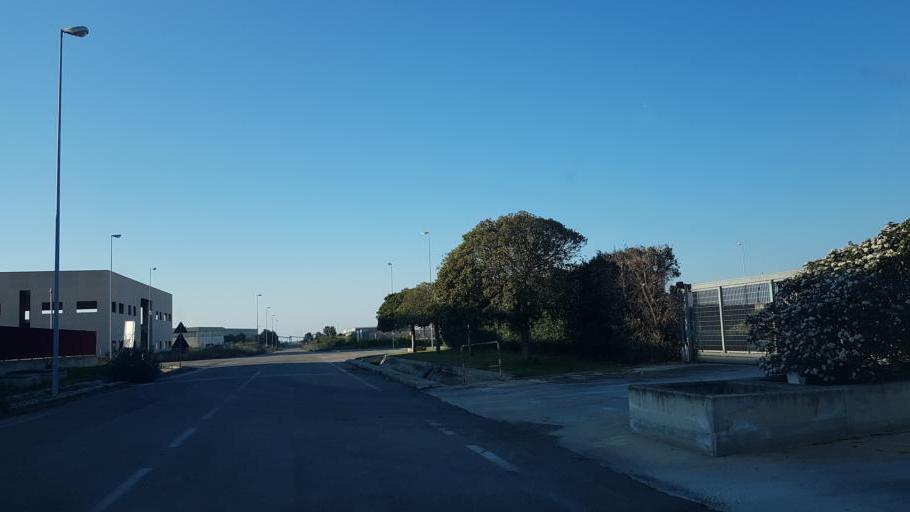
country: IT
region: Apulia
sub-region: Provincia di Brindisi
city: La Rosa
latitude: 40.6226
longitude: 17.9716
